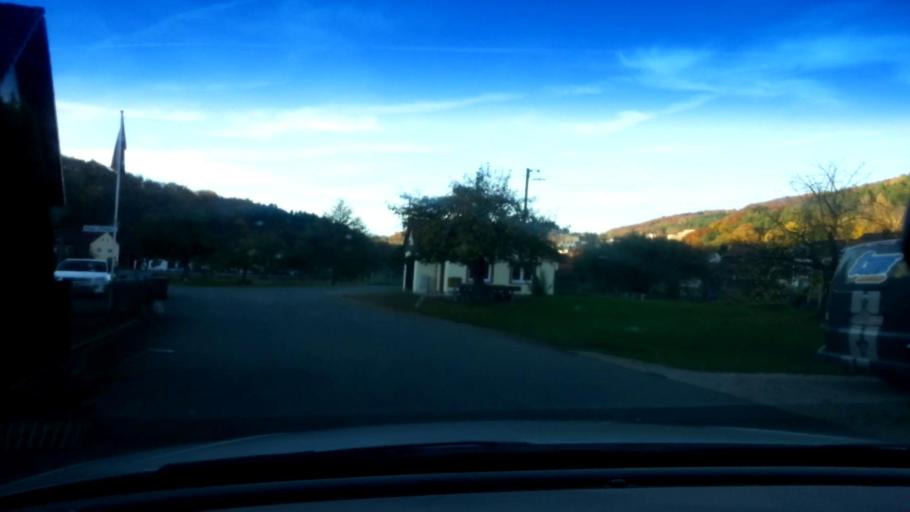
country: DE
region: Bavaria
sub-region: Upper Franconia
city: Heiligenstadt
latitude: 49.8562
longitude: 11.1769
